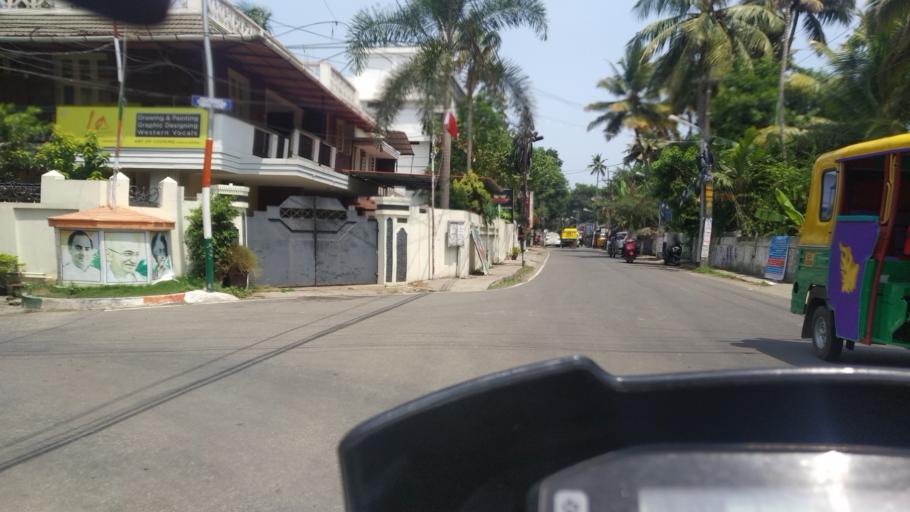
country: IN
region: Kerala
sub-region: Ernakulam
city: Cochin
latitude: 9.9543
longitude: 76.3023
